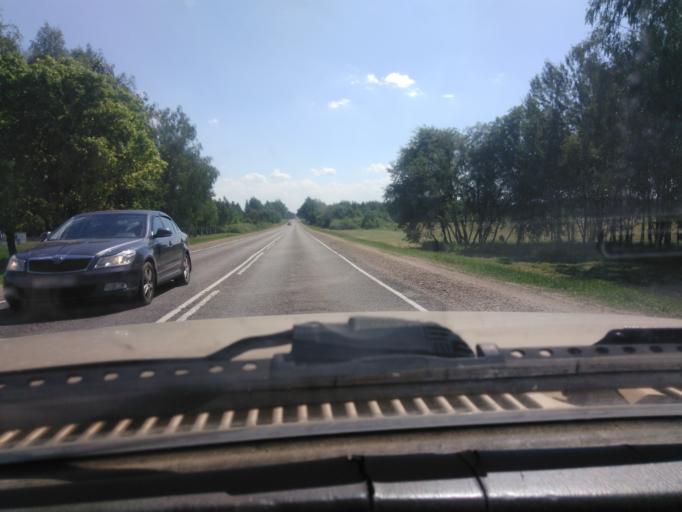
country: BY
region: Mogilev
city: Palykavichy Pyershyya
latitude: 54.0110
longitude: 30.3210
